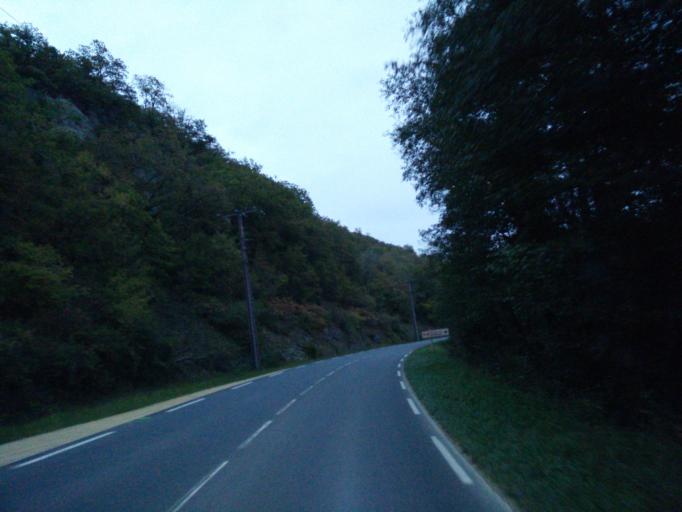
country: FR
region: Aquitaine
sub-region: Departement de la Dordogne
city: Saint-Cyprien
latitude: 44.9328
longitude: 1.0720
